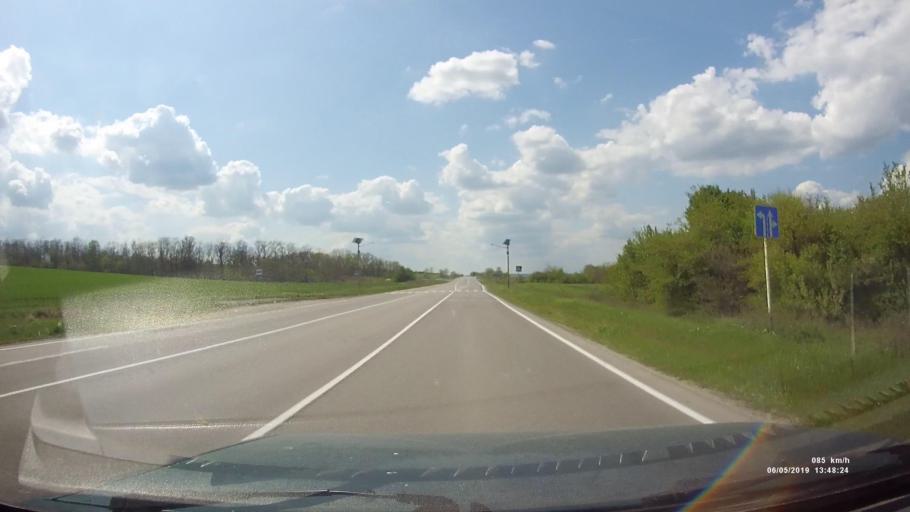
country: RU
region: Rostov
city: Melikhovskaya
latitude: 47.6586
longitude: 40.5443
